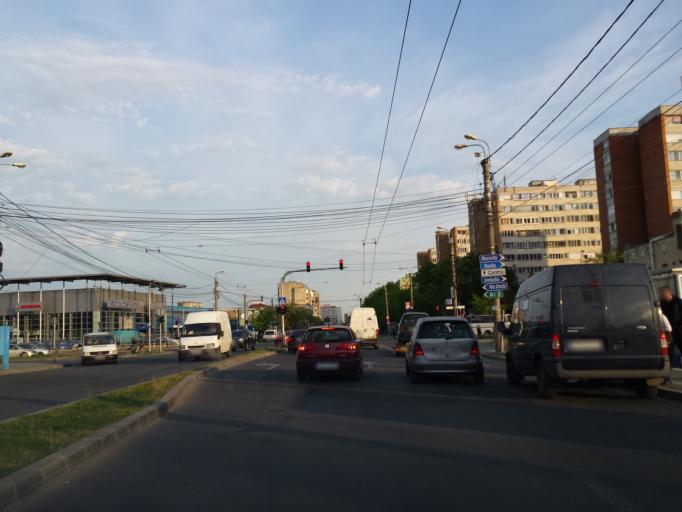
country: RO
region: Timis
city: Timisoara
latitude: 45.7695
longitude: 21.2197
